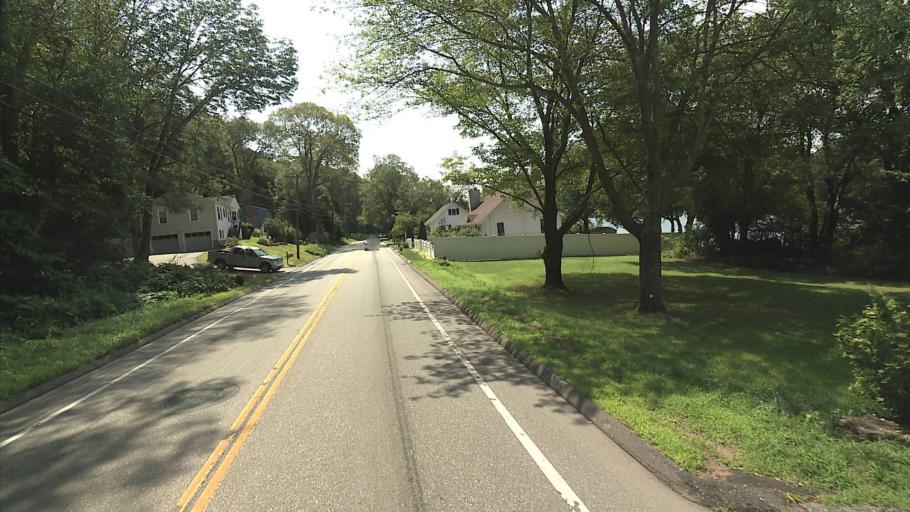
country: US
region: Connecticut
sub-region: New London County
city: Niantic
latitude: 41.3420
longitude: -72.2082
